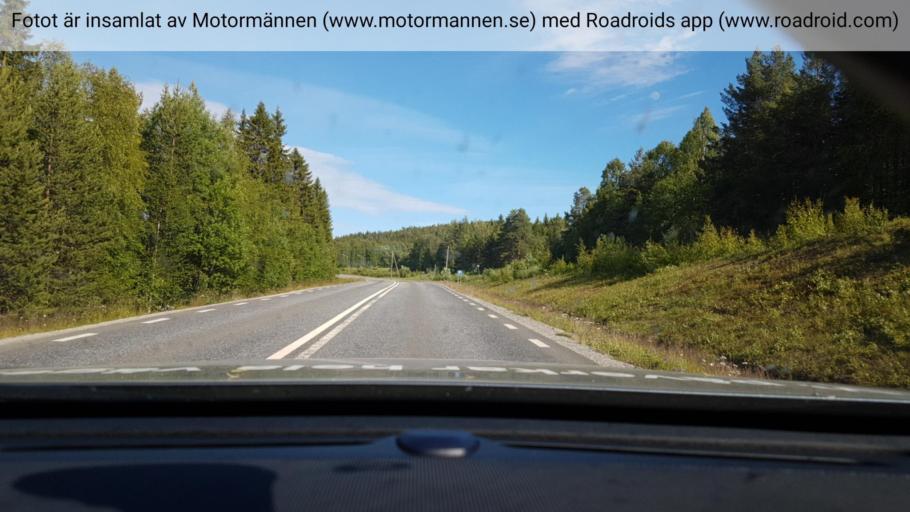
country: SE
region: Vaesterbotten
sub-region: Lycksele Kommun
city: Soderfors
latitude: 64.7045
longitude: 18.3261
